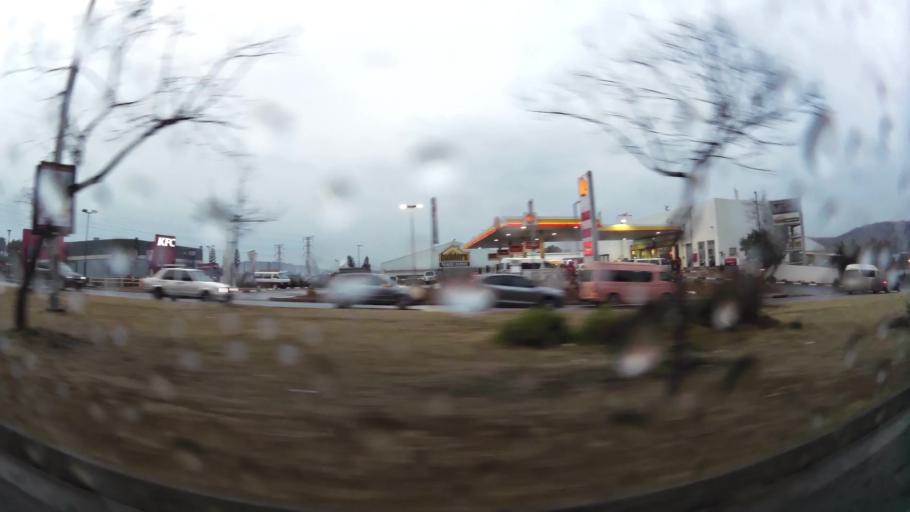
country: ZA
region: Gauteng
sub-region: City of Johannesburg Metropolitan Municipality
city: Soweto
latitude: -26.2591
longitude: 27.9294
